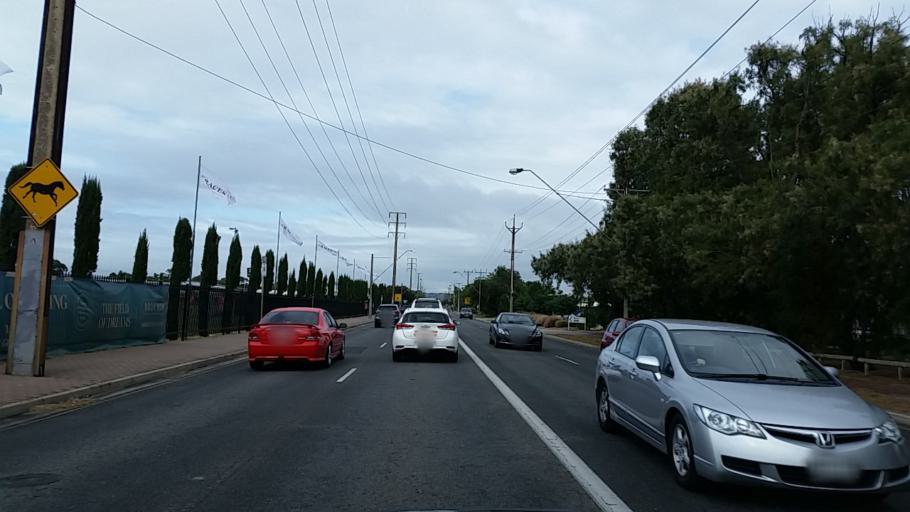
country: AU
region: South Australia
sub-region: Holdfast Bay
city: Glenelg East
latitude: -34.9783
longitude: 138.5380
